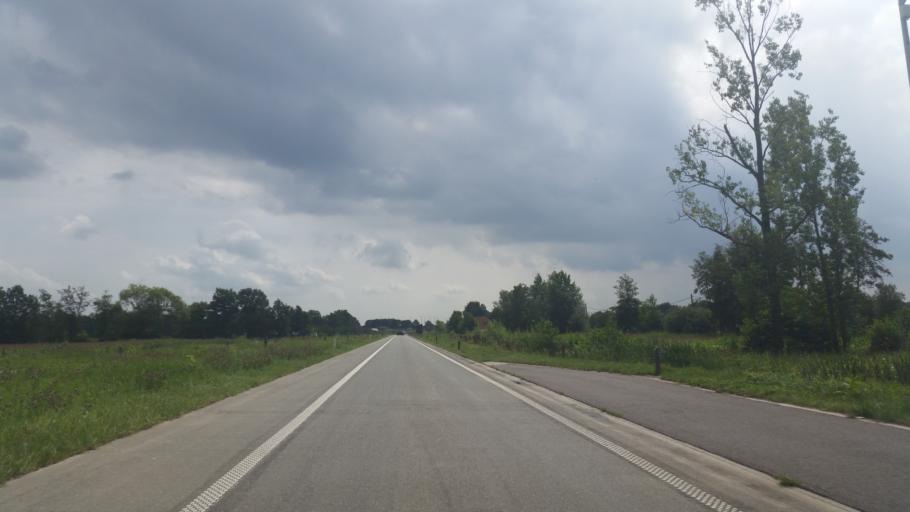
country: BE
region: Flanders
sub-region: Provincie Antwerpen
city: Geel
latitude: 51.1878
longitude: 4.9728
